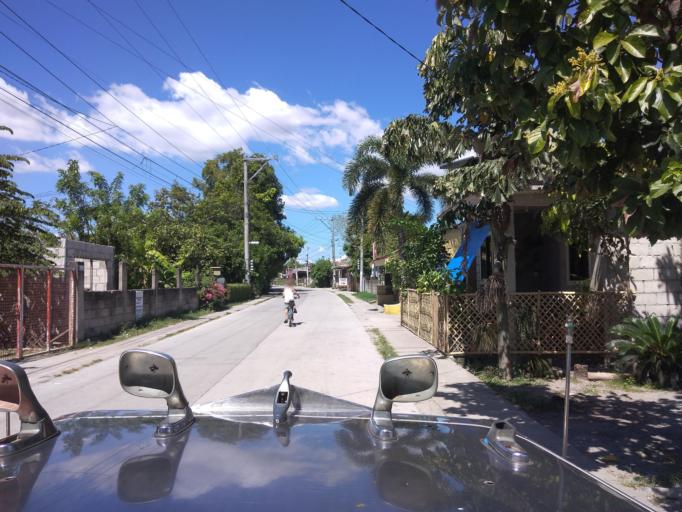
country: PH
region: Central Luzon
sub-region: Province of Pampanga
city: Magliman
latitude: 15.0415
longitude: 120.6448
